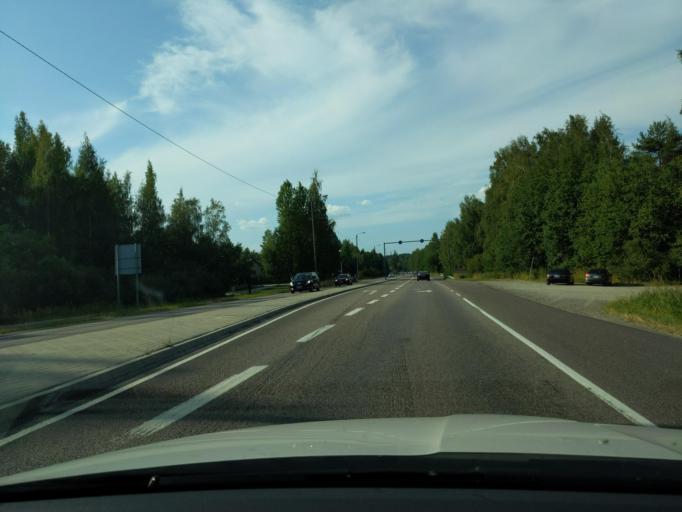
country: FI
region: Paijanne Tavastia
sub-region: Lahti
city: Lahti
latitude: 61.0200
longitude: 25.6781
